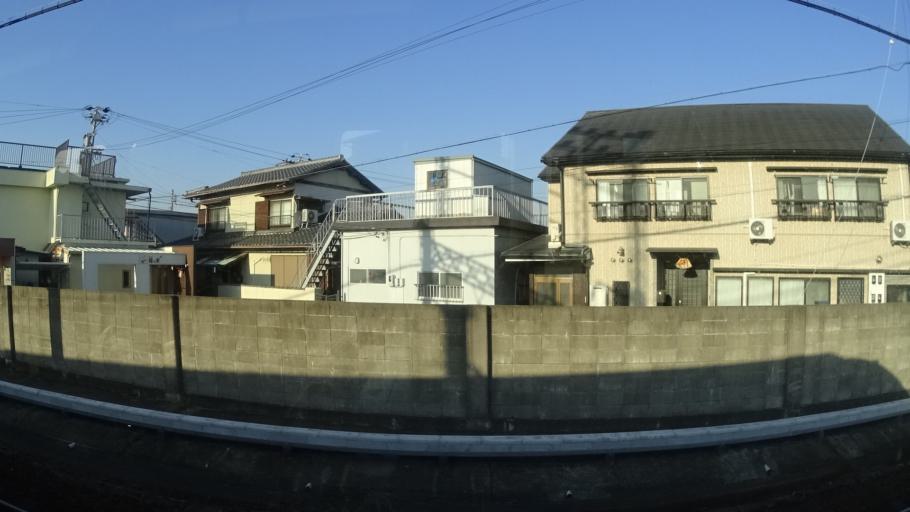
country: JP
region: Mie
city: Ise
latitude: 34.4989
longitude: 136.6971
